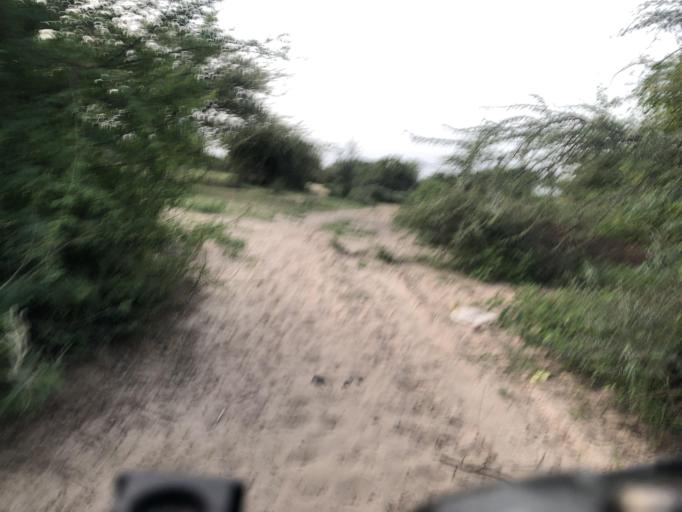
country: SN
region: Saint-Louis
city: Saint-Louis
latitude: 16.0613
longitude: -16.4324
